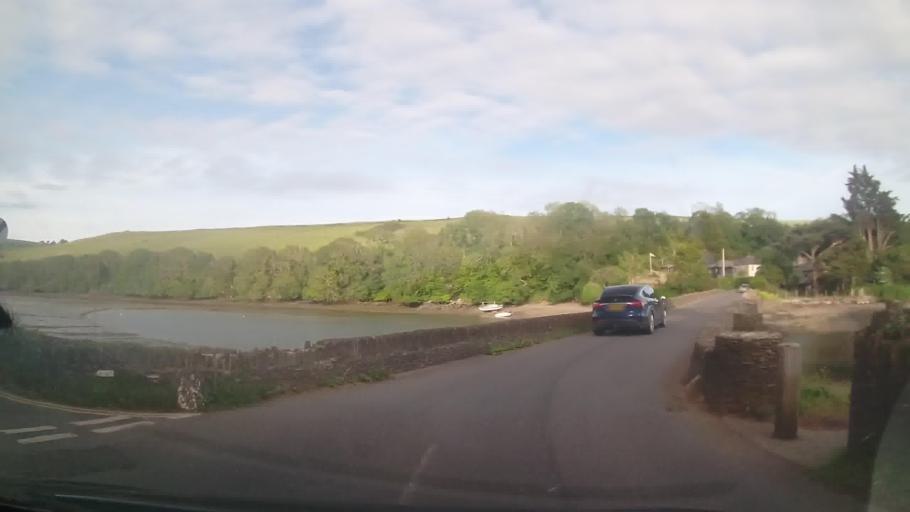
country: GB
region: England
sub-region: Devon
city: Kingsbridge
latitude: 50.2751
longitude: -3.7628
